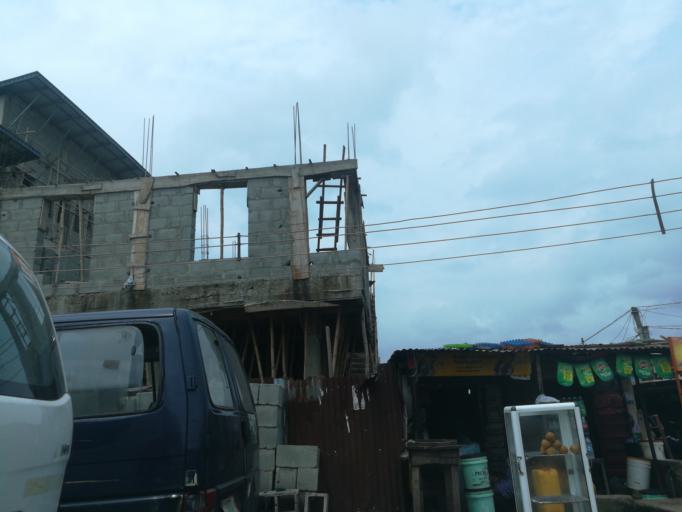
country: NG
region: Lagos
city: Ojota
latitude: 6.5709
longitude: 3.3627
